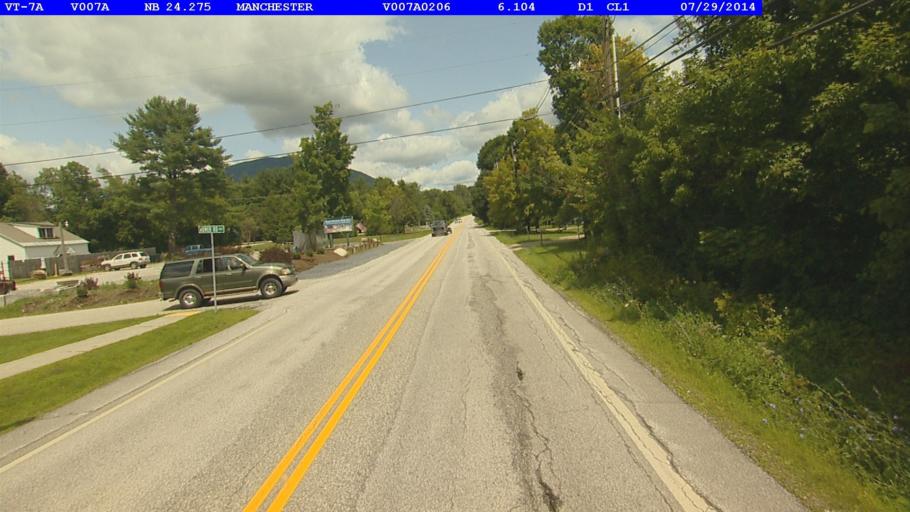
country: US
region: Vermont
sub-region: Bennington County
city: Manchester Center
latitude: 43.1893
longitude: -73.0428
